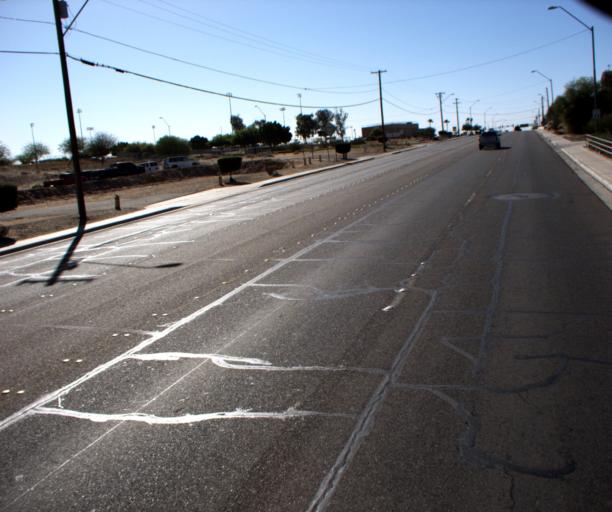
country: US
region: Arizona
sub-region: Yuma County
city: San Luis
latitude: 32.4980
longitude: -114.7855
